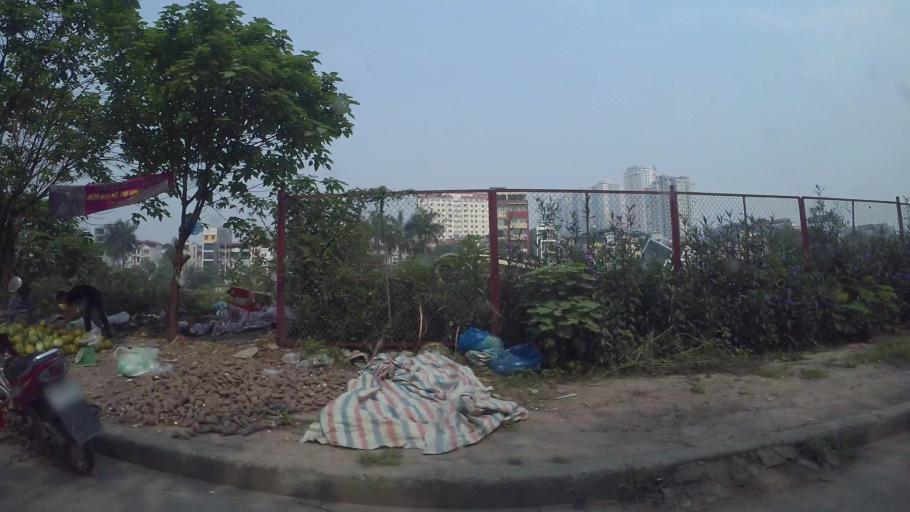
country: VN
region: Ha Noi
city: Van Dien
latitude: 20.9675
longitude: 105.8239
